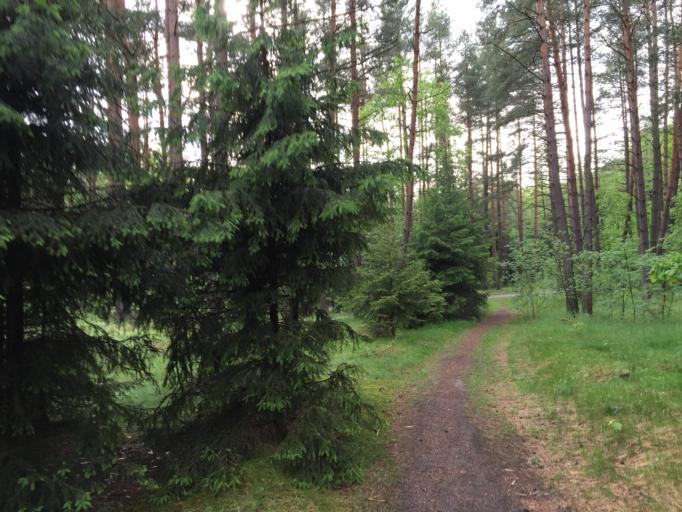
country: LT
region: Klaipedos apskritis
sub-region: Klaipeda
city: Klaipeda
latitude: 55.7483
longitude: 21.1200
